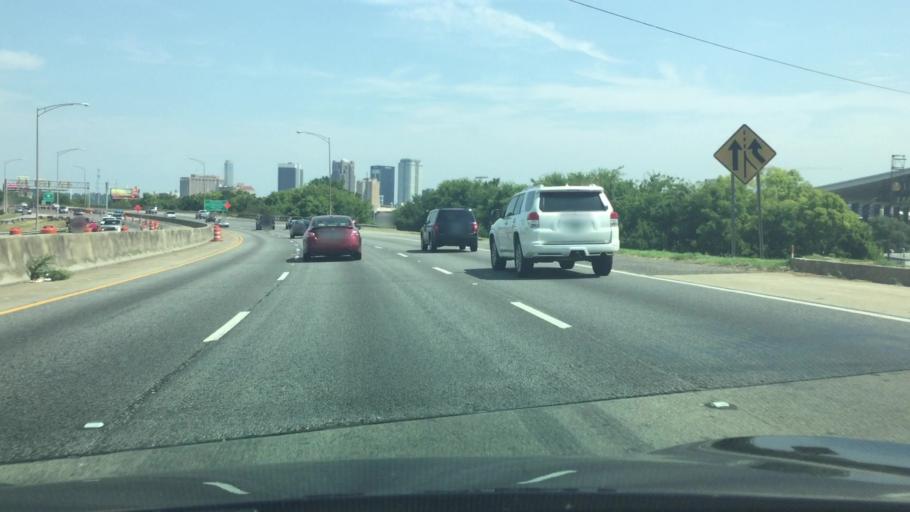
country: US
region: Alabama
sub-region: Jefferson County
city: Birmingham
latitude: 33.4990
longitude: -86.8143
